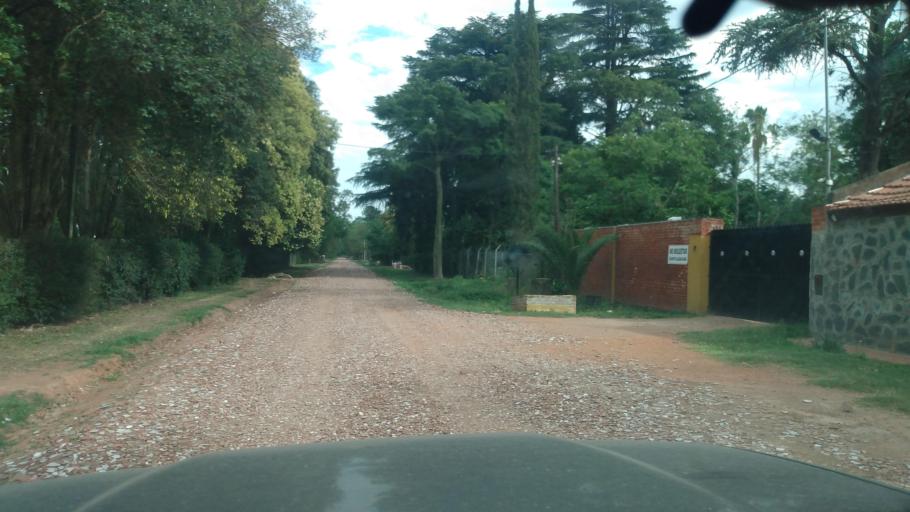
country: AR
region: Buenos Aires
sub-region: Partido de Lujan
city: Lujan
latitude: -34.5949
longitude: -59.0532
